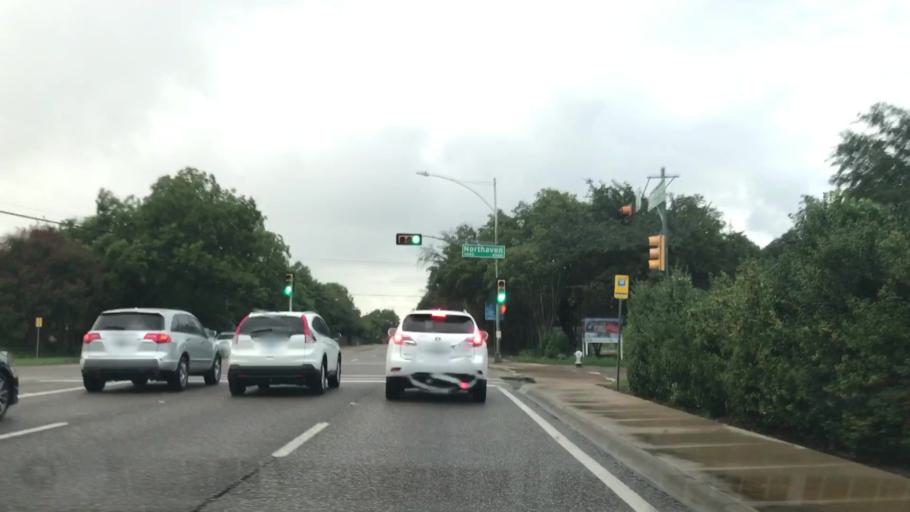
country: US
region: Texas
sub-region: Dallas County
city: University Park
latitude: 32.9019
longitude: -96.8039
